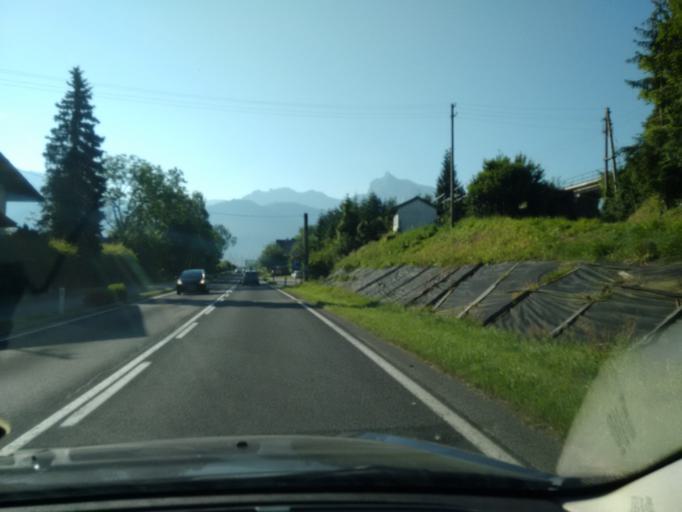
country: AT
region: Upper Austria
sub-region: Politischer Bezirk Gmunden
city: Altmunster
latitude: 47.8629
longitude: 13.7774
